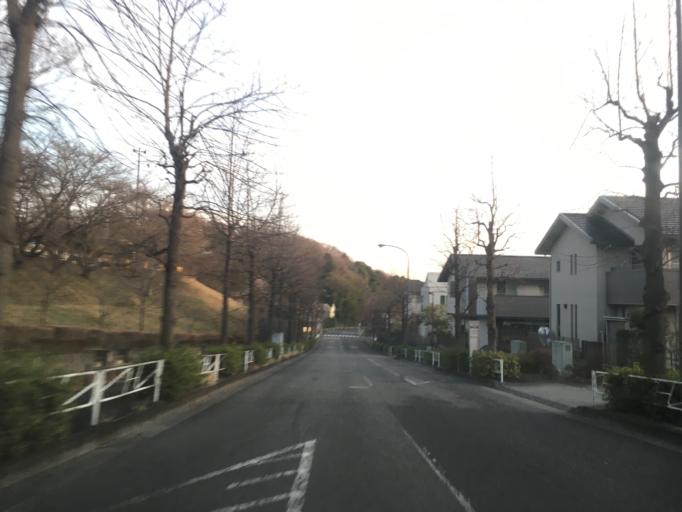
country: JP
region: Tokyo
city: Hachioji
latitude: 35.6100
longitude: 139.3570
